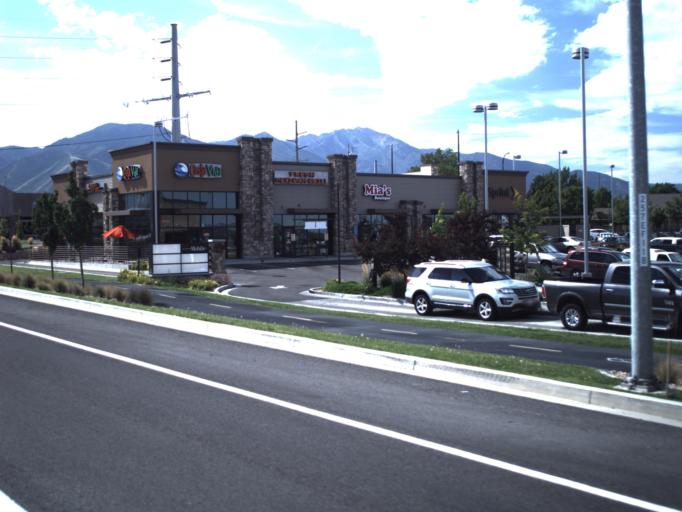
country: US
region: Utah
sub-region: Utah County
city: Spanish Fork
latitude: 40.1238
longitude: -111.6445
